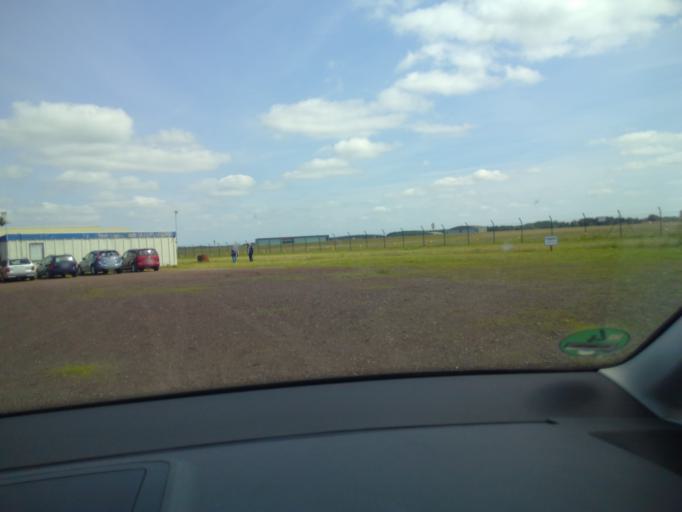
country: DE
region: Lower Saxony
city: Midlum
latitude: 53.7672
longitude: 8.6360
